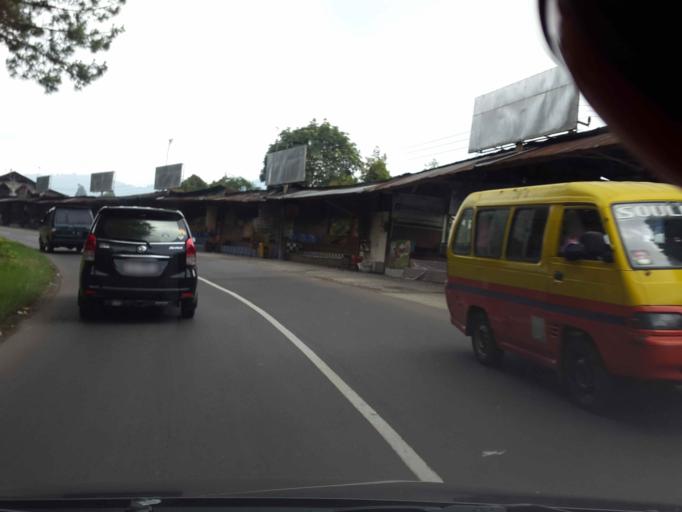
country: ID
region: West Java
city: Lembang
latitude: -6.8055
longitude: 107.6486
